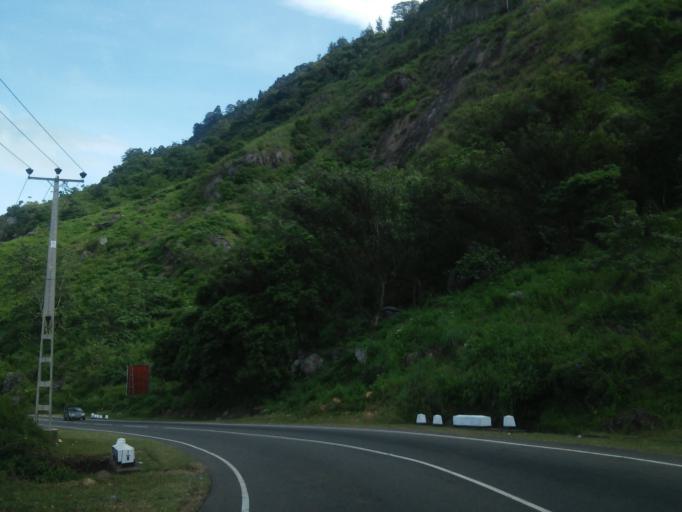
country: LK
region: Uva
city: Haputale
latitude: 6.7636
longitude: 80.9183
